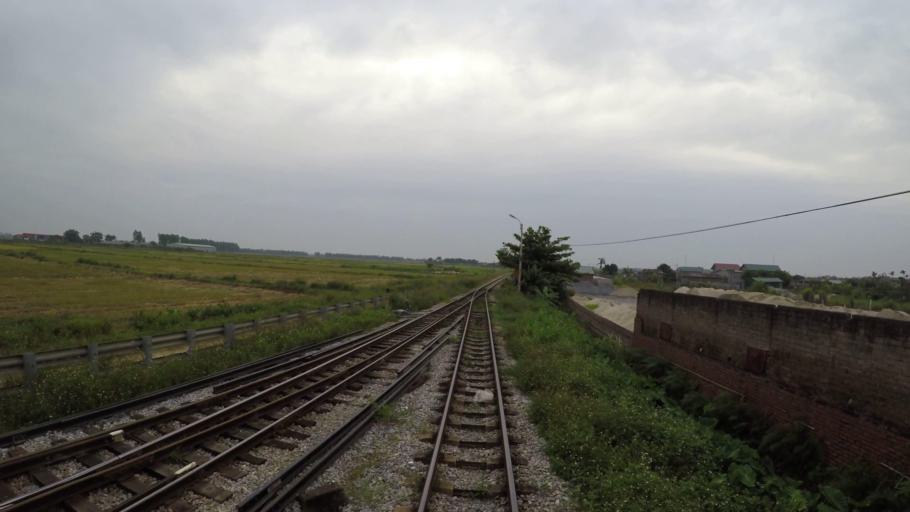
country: VN
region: Bac Ninh
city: Thua
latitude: 20.9673
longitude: 106.1703
